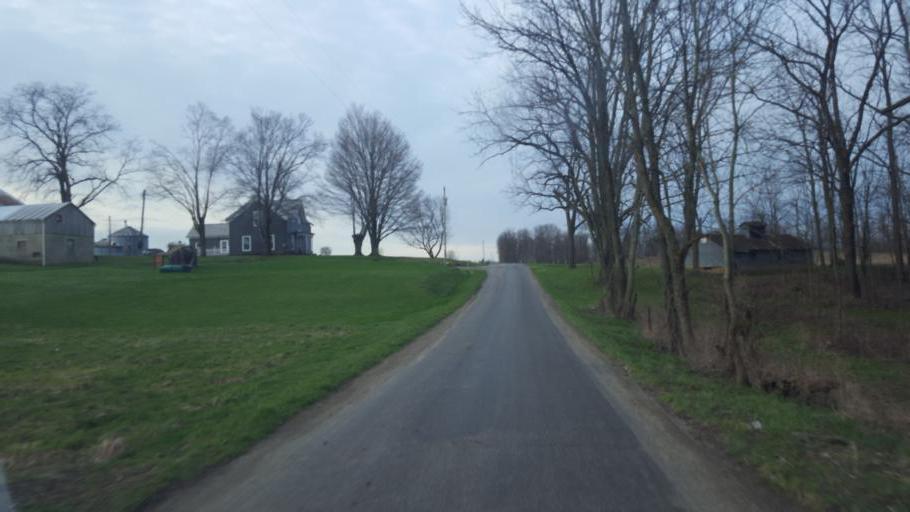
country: US
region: Ohio
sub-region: Knox County
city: Fredericktown
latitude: 40.5534
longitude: -82.5855
